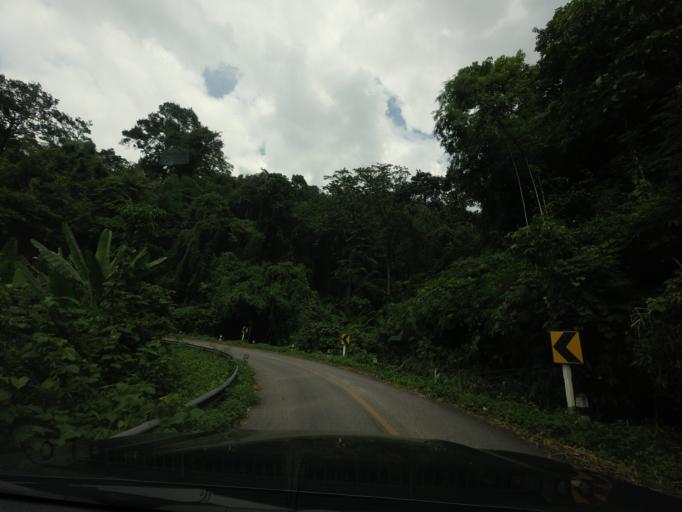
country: TH
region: Loei
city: Na Haeo
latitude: 17.7181
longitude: 100.9484
